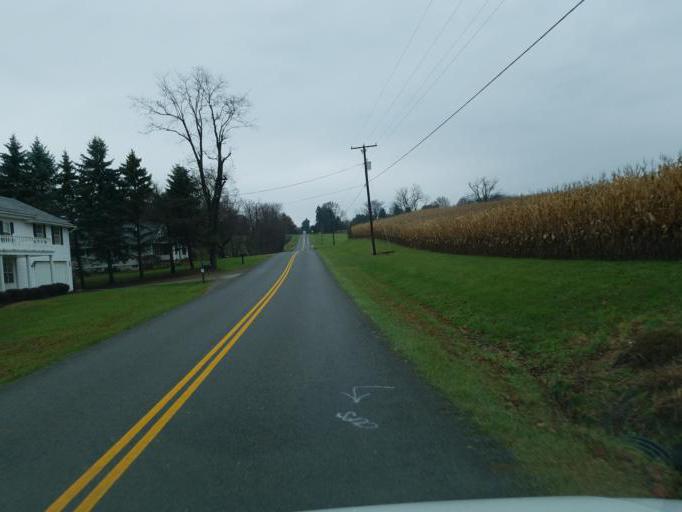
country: US
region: Ohio
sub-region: Richland County
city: Lexington
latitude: 40.7178
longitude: -82.5991
